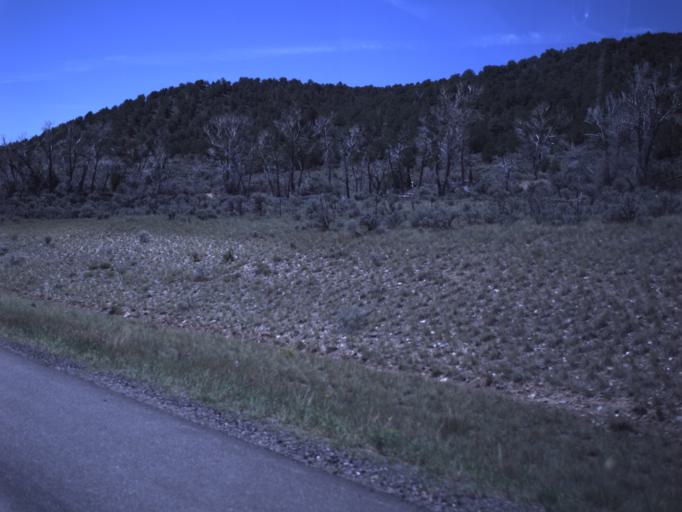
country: US
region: Utah
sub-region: Garfield County
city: Panguitch
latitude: 37.8092
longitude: -112.4022
